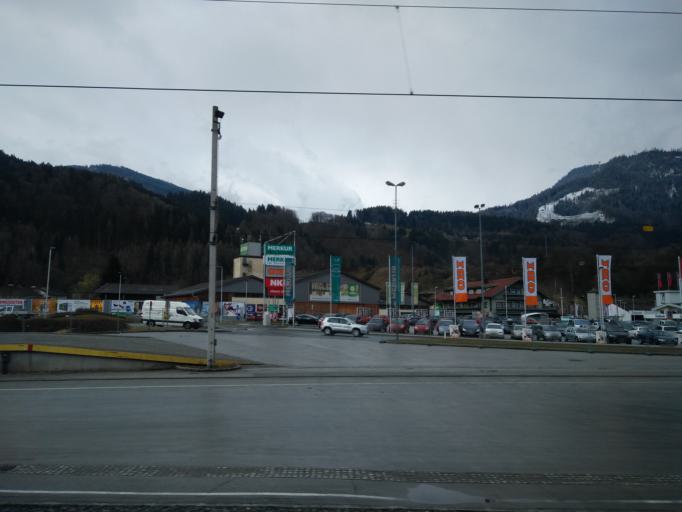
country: AT
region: Salzburg
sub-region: Politischer Bezirk Sankt Johann im Pongau
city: Bischofshofen
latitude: 47.4099
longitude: 13.2180
